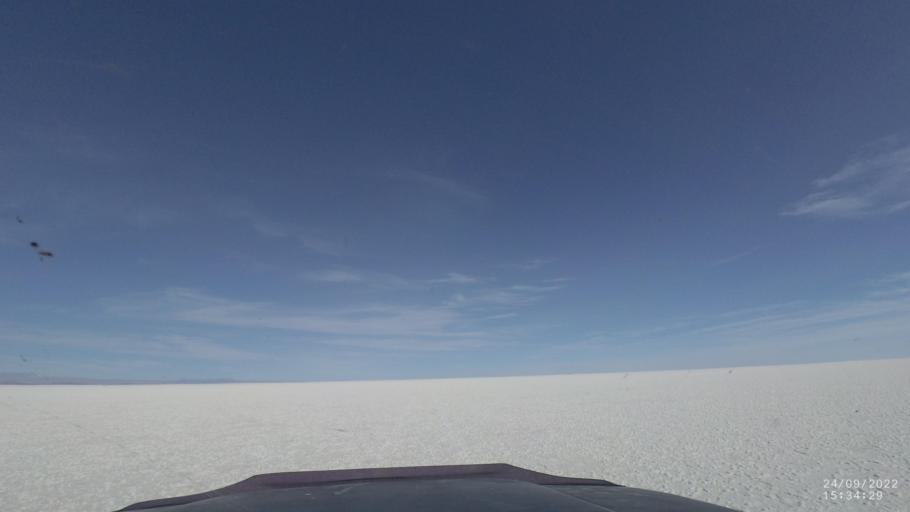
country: BO
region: Potosi
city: Colchani
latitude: -20.1250
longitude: -67.2621
